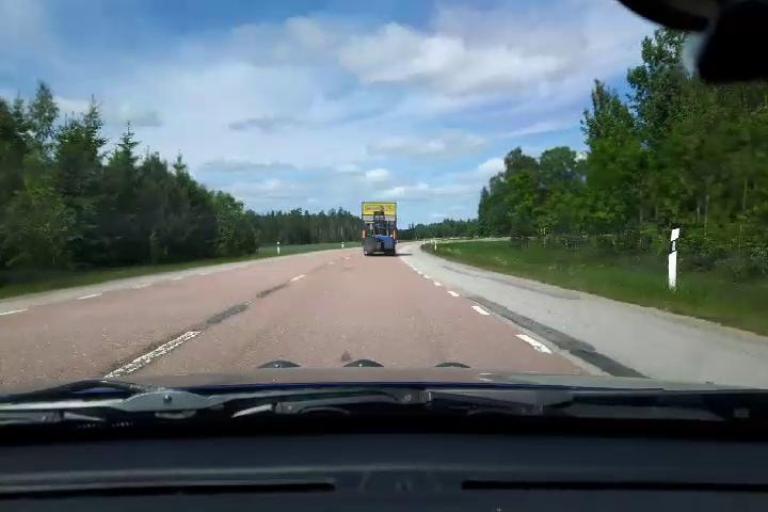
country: SE
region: Uppsala
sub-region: Osthammars Kommun
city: Bjorklinge
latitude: 60.1542
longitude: 17.4914
